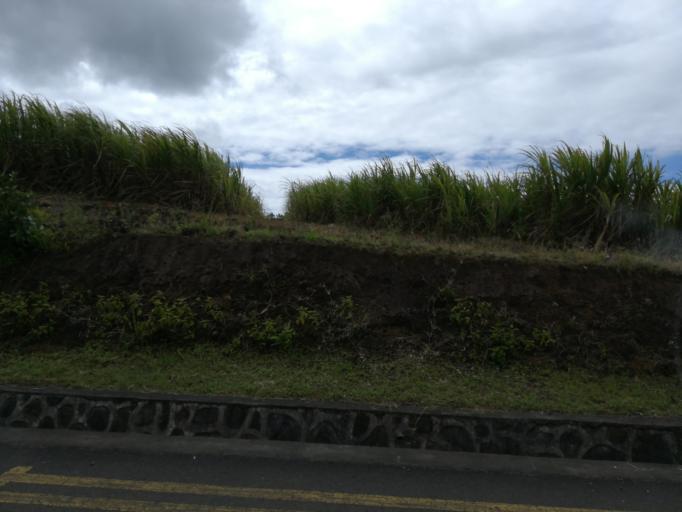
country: MU
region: Moka
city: Providence
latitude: -20.2447
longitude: 57.6034
